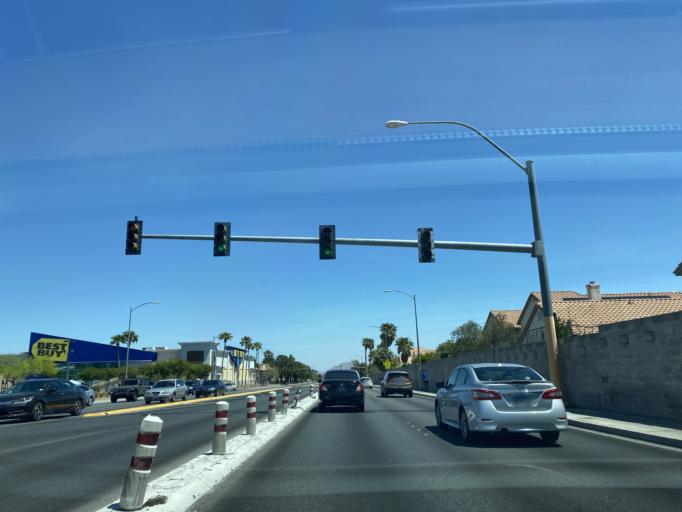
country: US
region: Nevada
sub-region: Clark County
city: Spring Valley
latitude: 36.1959
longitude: -115.2401
